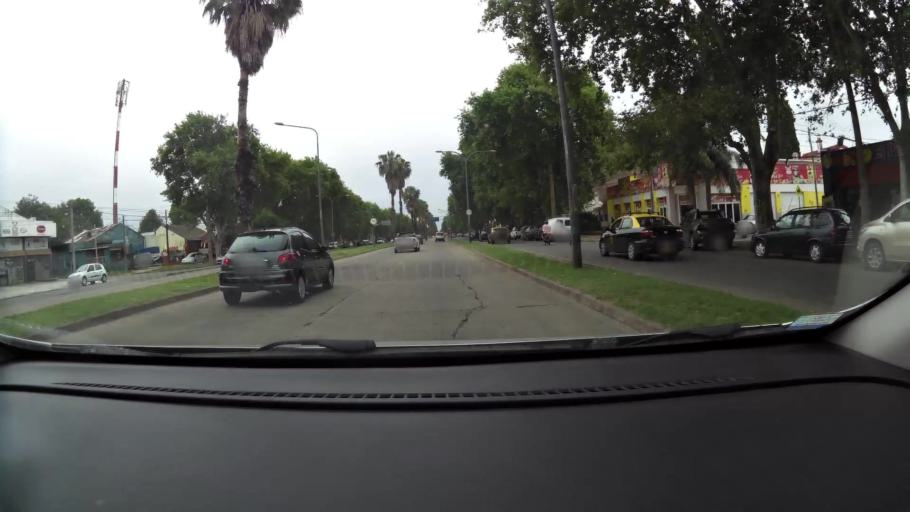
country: AR
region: Santa Fe
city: Granadero Baigorria
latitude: -32.8877
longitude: -60.6945
